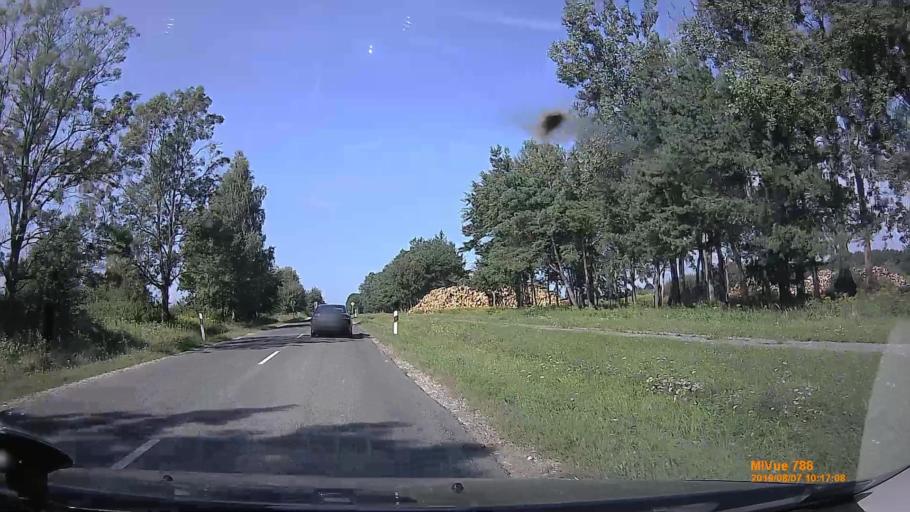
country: HU
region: Zala
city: Lenti
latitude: 46.6358
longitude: 16.5838
